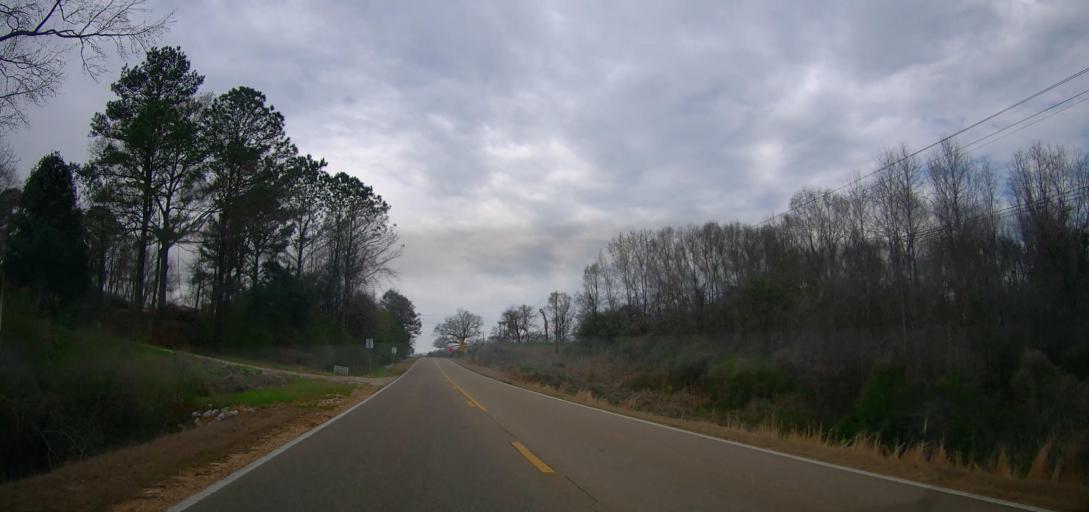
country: US
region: Mississippi
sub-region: Itawamba County
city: Fulton
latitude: 34.2777
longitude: -88.3654
